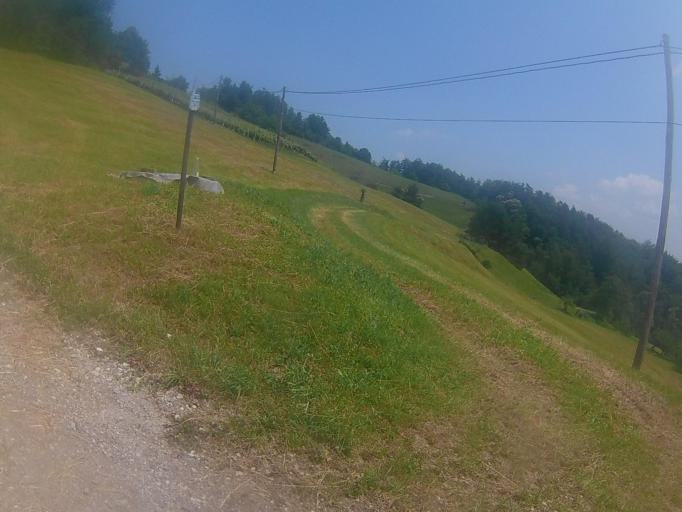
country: SI
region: Maribor
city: Kamnica
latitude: 46.5963
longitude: 15.6000
